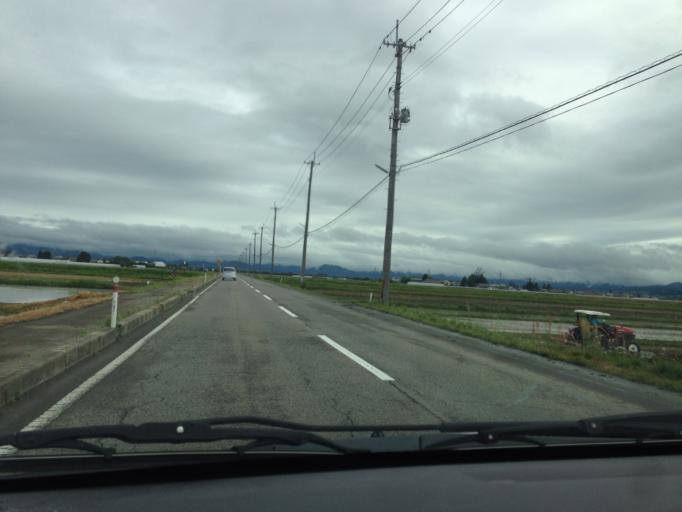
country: JP
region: Fukushima
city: Kitakata
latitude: 37.5472
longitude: 139.8559
